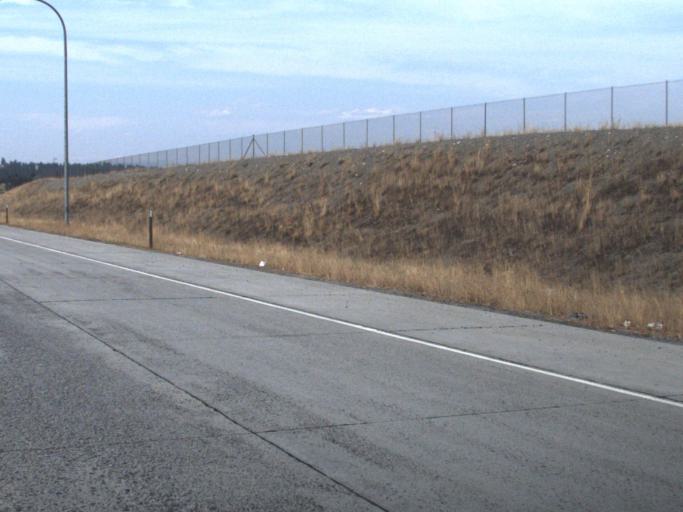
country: US
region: Washington
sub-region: Spokane County
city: Mead
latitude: 47.7590
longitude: -117.3646
